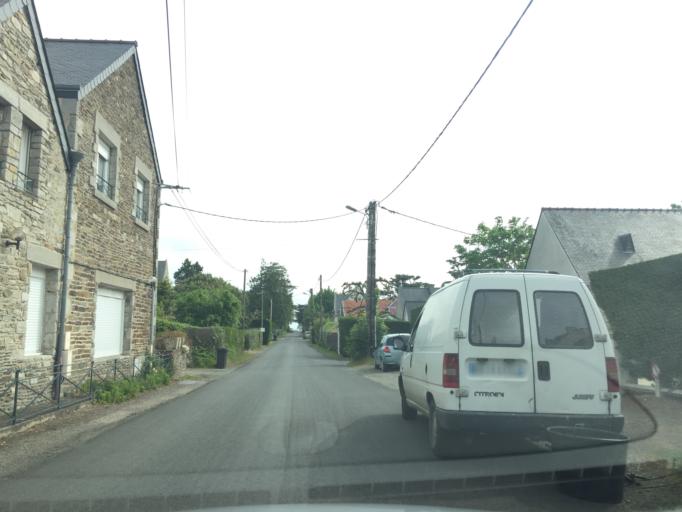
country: FR
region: Brittany
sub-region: Departement des Cotes-d'Armor
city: Saint-Cast-le-Guildo
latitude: 48.6213
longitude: -2.2456
